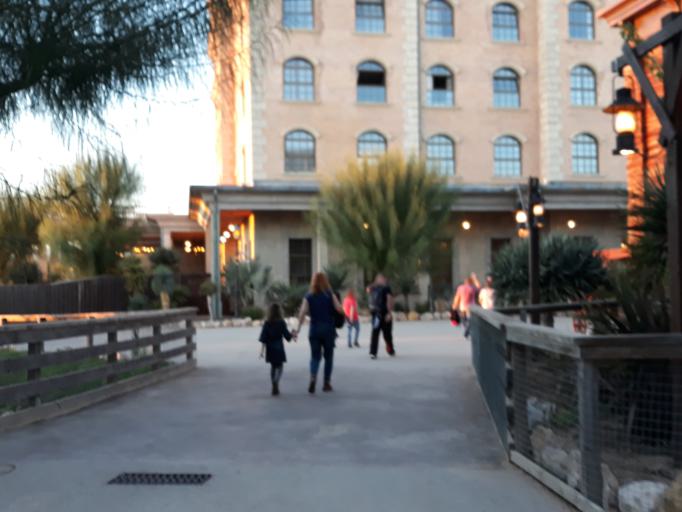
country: ES
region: Catalonia
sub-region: Provincia de Tarragona
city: Salou
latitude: 41.0915
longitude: 1.1545
